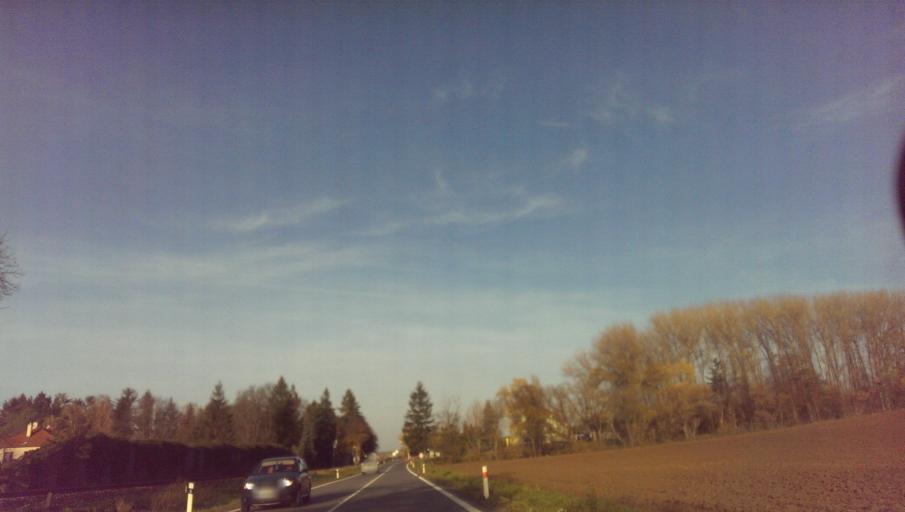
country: CZ
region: Zlin
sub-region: Okres Zlin
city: Ostrozska Nova Ves
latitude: 49.0161
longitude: 17.4442
